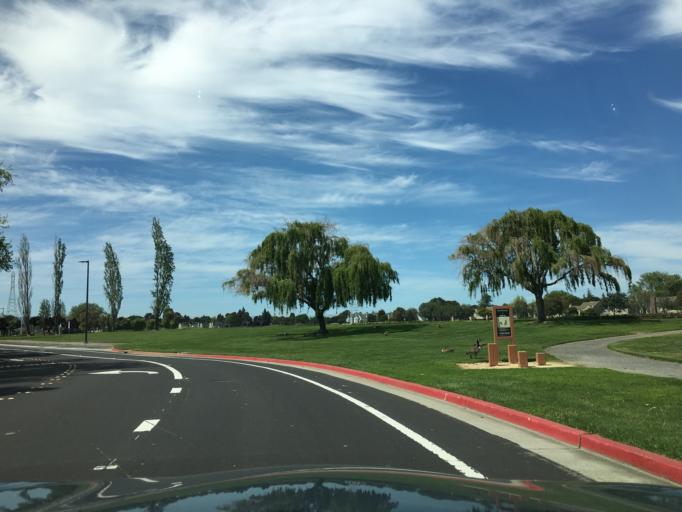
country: US
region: California
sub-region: San Mateo County
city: Redwood Shores
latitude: 37.5319
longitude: -122.2614
